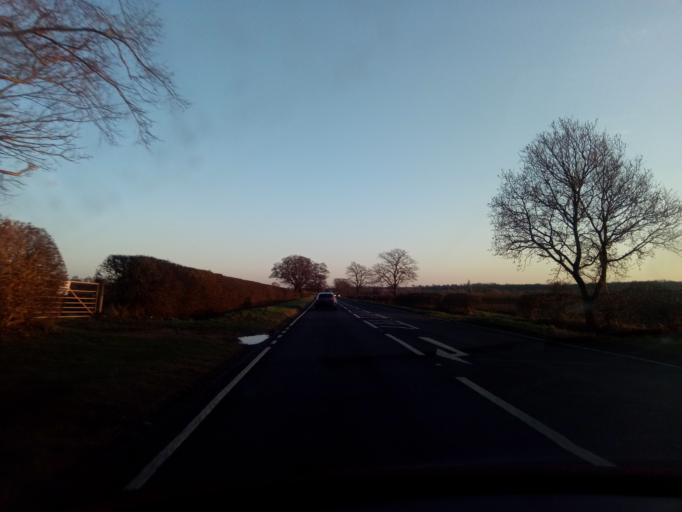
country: GB
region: England
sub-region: Nottinghamshire
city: Burton Joyce
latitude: 53.0394
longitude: -1.0541
